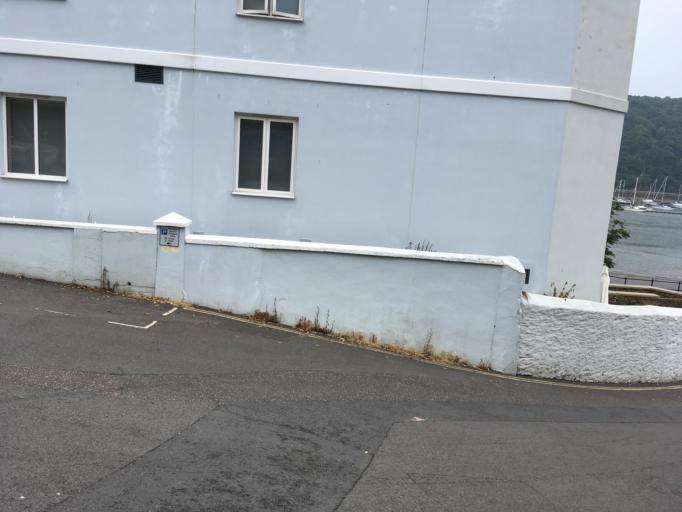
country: GB
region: England
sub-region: Devon
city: Dartmouth
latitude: 50.3568
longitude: -3.5776
